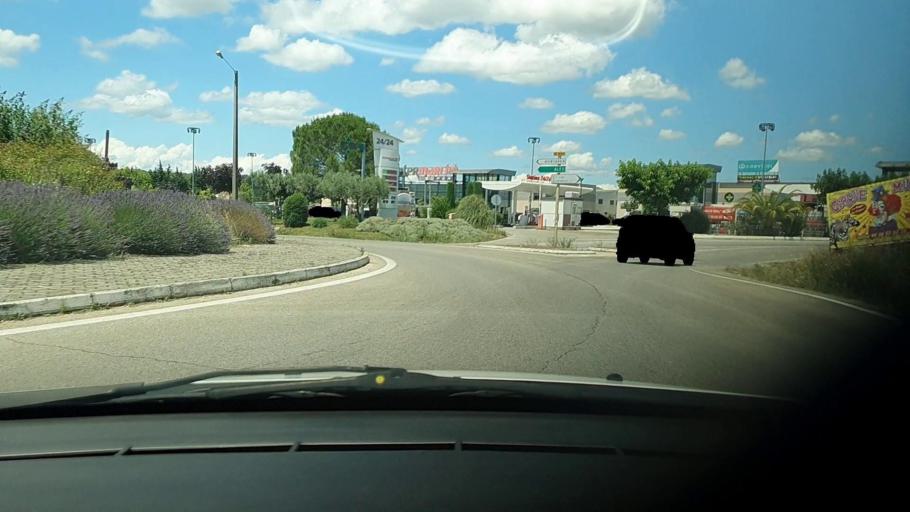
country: FR
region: Languedoc-Roussillon
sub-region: Departement du Gard
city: Montaren-et-Saint-Mediers
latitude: 44.0247
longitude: 4.3891
